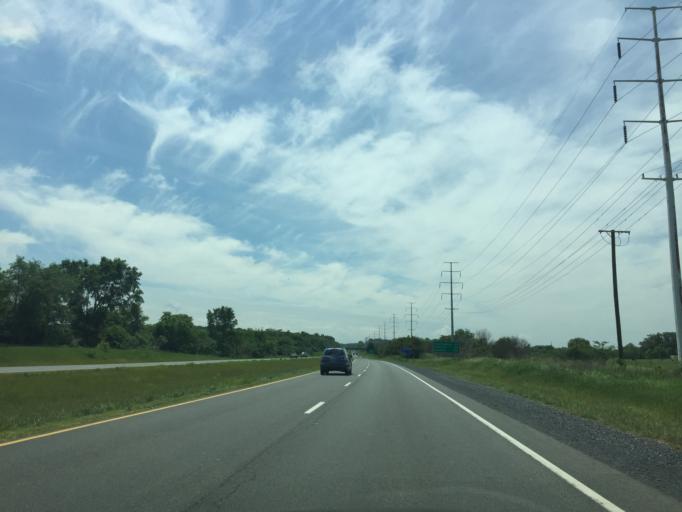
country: US
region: Virginia
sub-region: City of Winchester
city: Winchester
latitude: 39.1809
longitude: -78.2053
